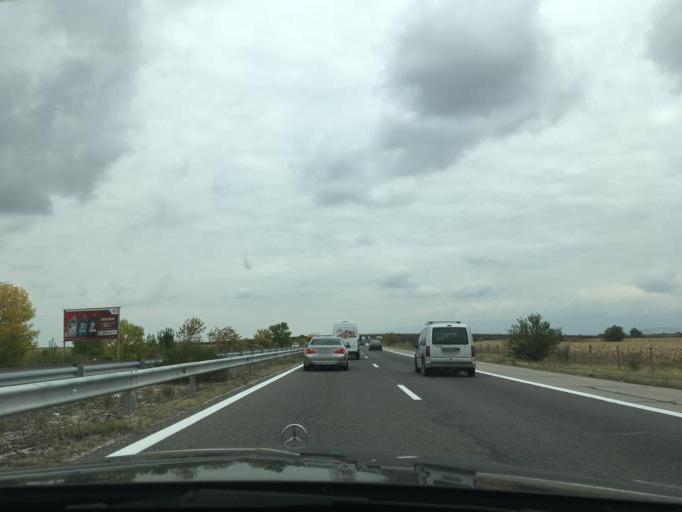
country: BG
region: Pazardzhik
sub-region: Obshtina Pazardzhik
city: Pazardzhik
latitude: 42.2473
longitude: 24.3507
